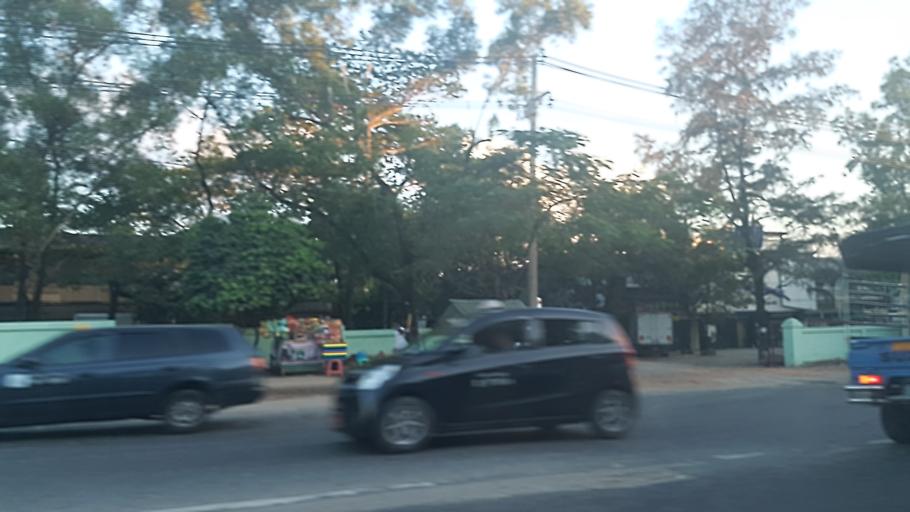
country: MM
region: Yangon
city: Yangon
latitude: 16.8946
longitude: 96.1209
